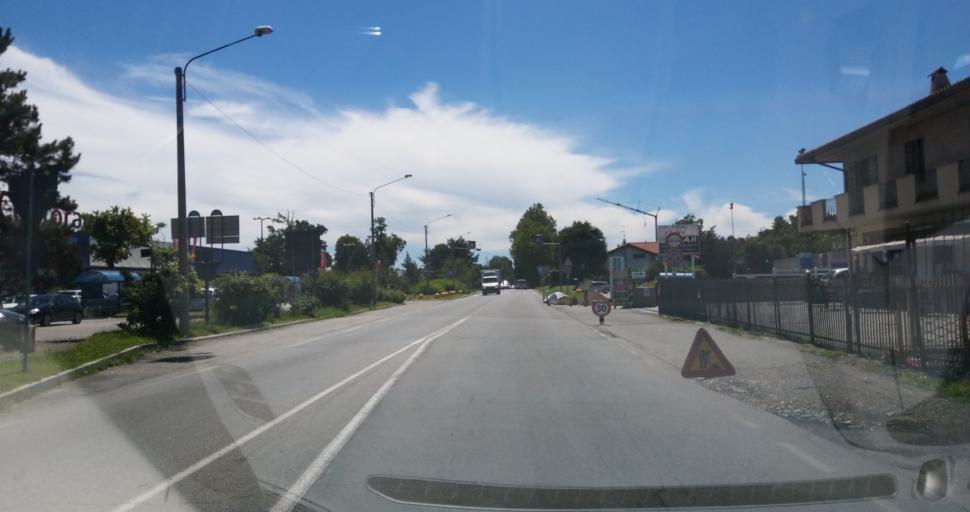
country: IT
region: Lombardy
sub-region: Provincia di Varese
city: Vergiate
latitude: 45.7180
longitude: 8.6910
